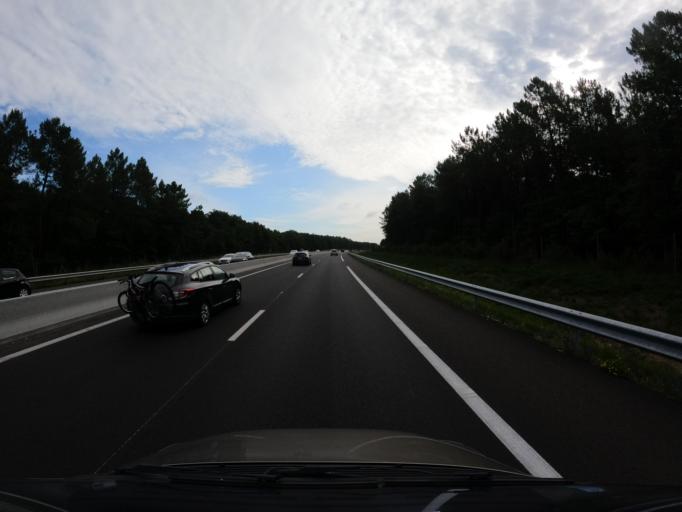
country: FR
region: Centre
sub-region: Departement d'Indre-et-Loire
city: Langeais
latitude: 47.3421
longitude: 0.3562
